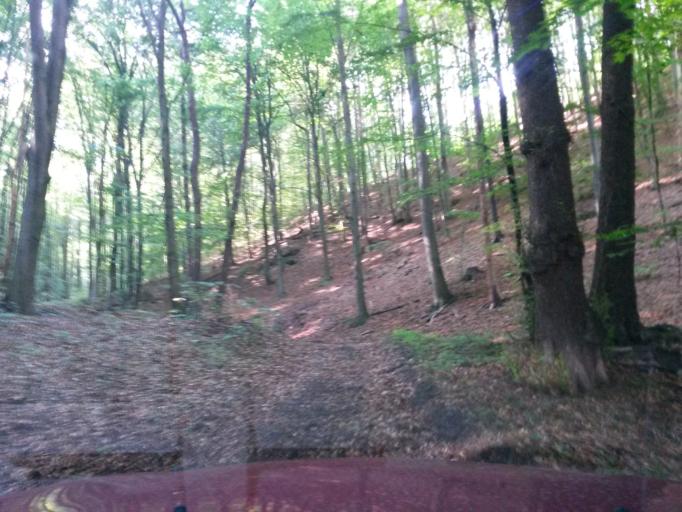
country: SK
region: Kosicky
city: Moldava nad Bodvou
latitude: 48.7274
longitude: 21.0761
